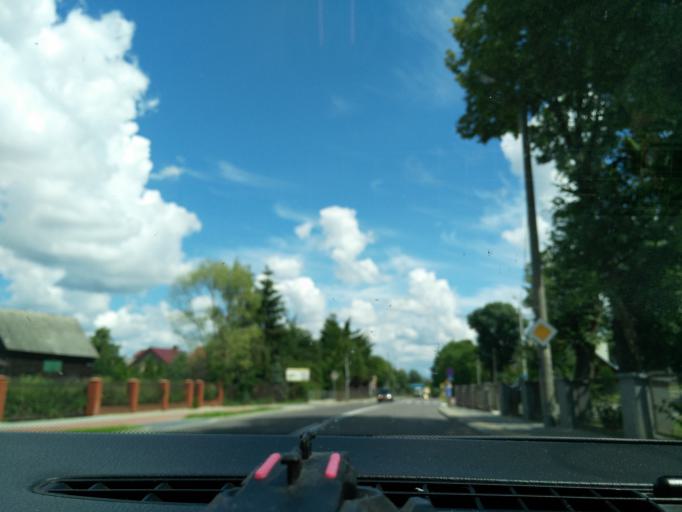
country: PL
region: Podlasie
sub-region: Powiat bielski
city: Bielsk Podlaski
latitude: 52.7592
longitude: 23.1784
